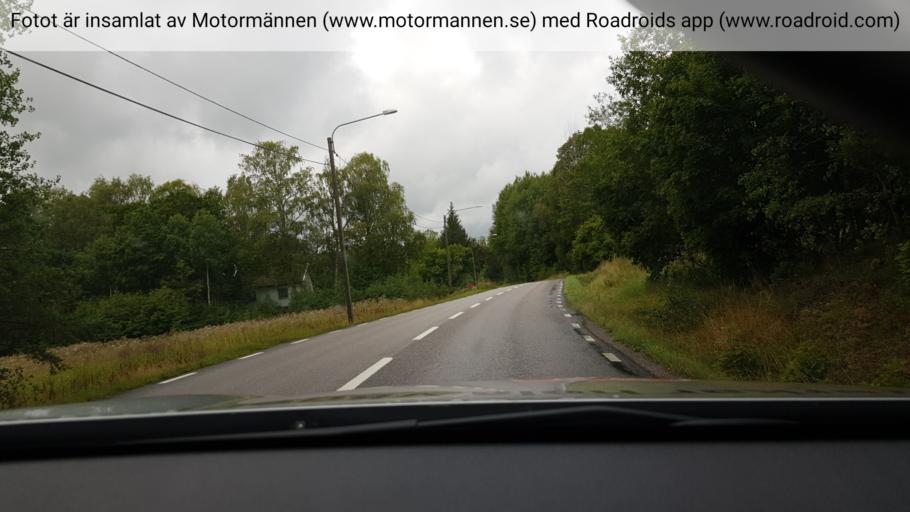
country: SE
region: Stockholm
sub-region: Norrtalje Kommun
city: Rimbo
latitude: 59.7354
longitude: 18.4076
